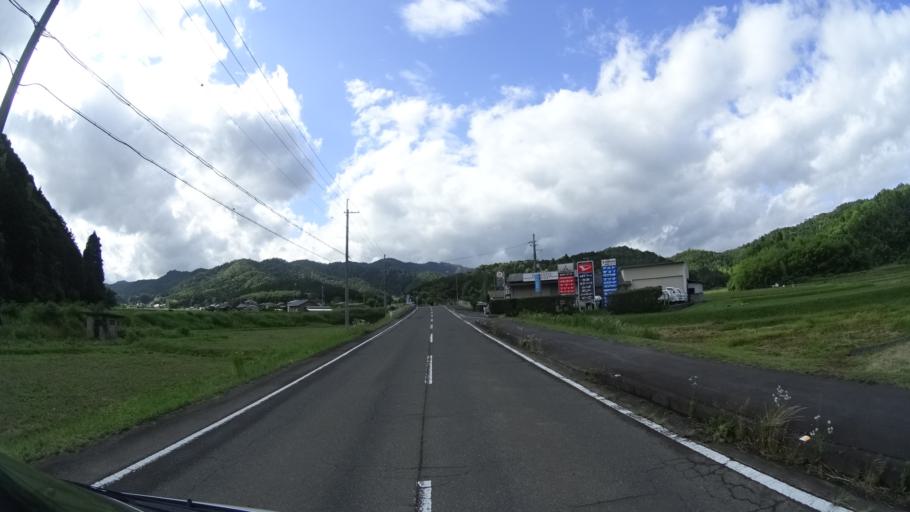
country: JP
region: Kyoto
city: Ayabe
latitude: 35.3722
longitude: 135.2399
